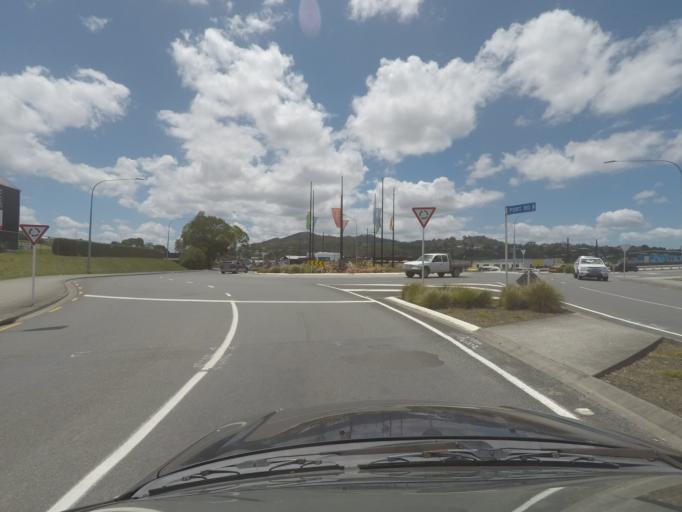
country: NZ
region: Northland
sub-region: Whangarei
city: Whangarei
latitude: -35.7354
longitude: 174.3329
